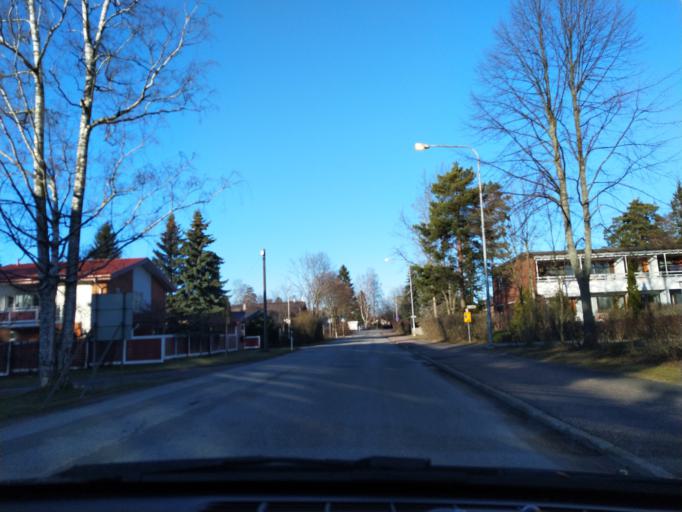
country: FI
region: Uusimaa
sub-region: Helsinki
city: Vantaa
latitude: 60.3017
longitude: 25.0394
